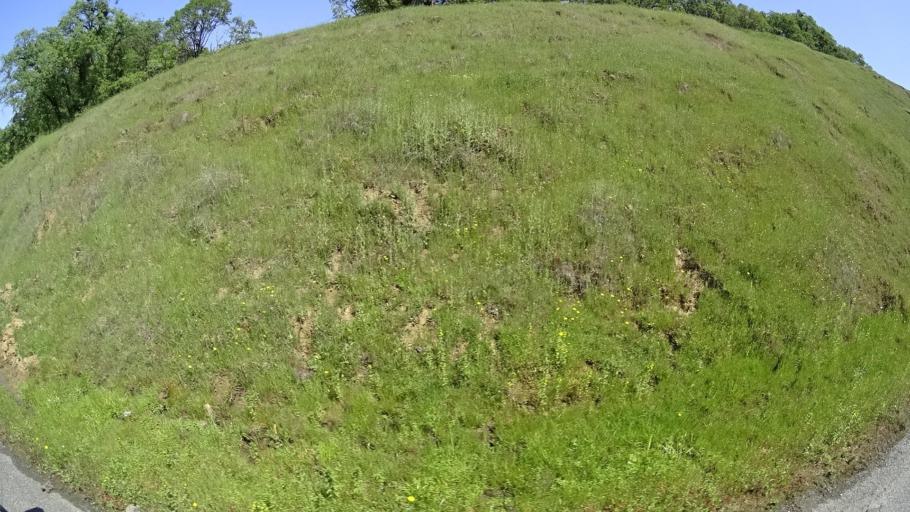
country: US
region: California
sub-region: Humboldt County
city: Redway
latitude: 40.2103
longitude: -123.5954
